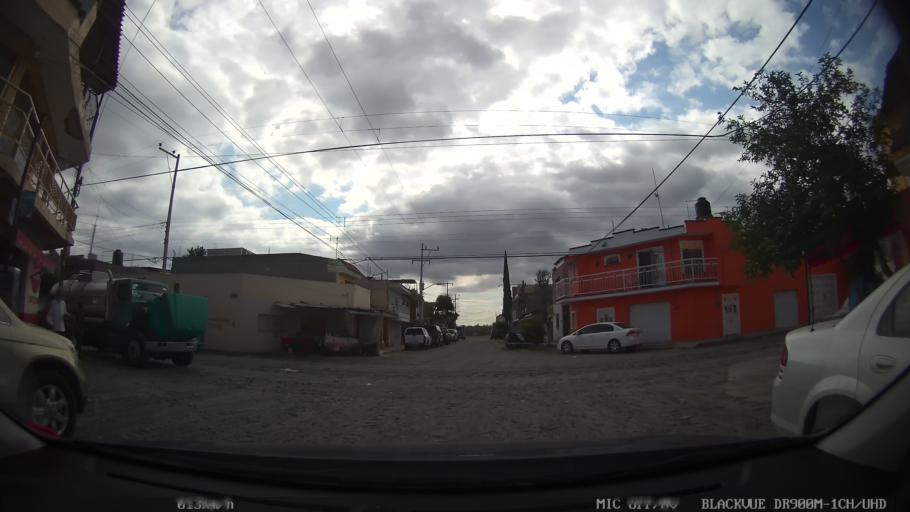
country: MX
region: Jalisco
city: Tlaquepaque
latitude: 20.6793
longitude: -103.2567
